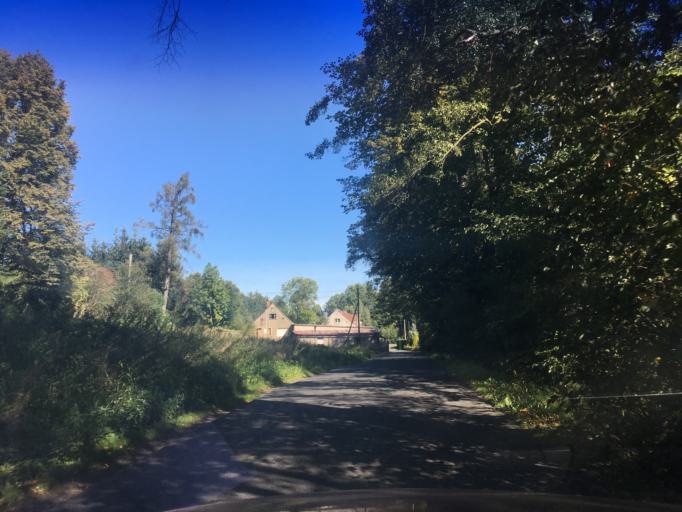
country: PL
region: Lower Silesian Voivodeship
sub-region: Powiat lubanski
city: Lesna
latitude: 51.0253
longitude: 15.2178
